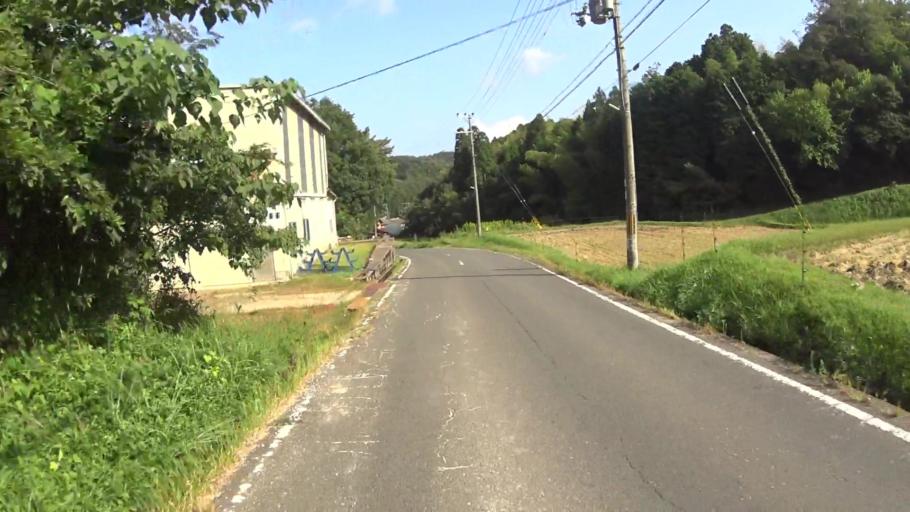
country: JP
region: Kyoto
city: Miyazu
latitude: 35.5724
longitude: 135.1128
